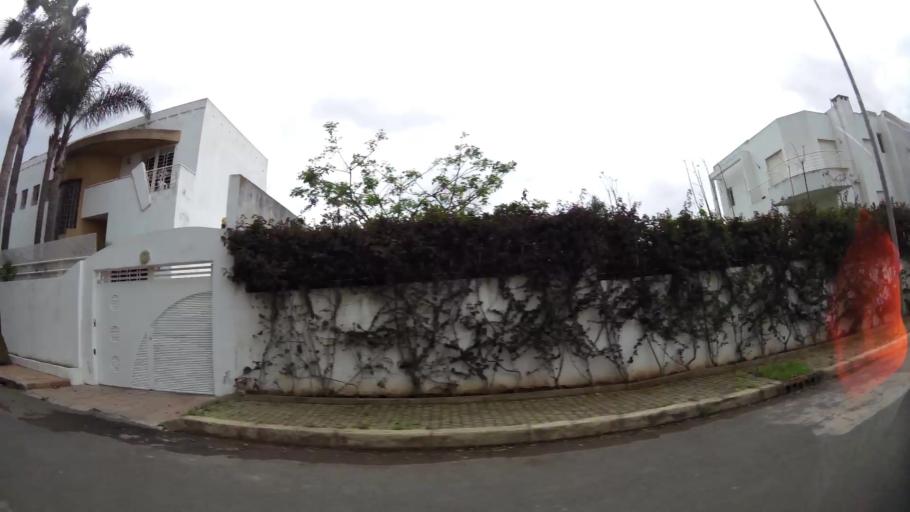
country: MA
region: Grand Casablanca
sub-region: Casablanca
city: Casablanca
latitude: 33.5343
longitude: -7.6334
